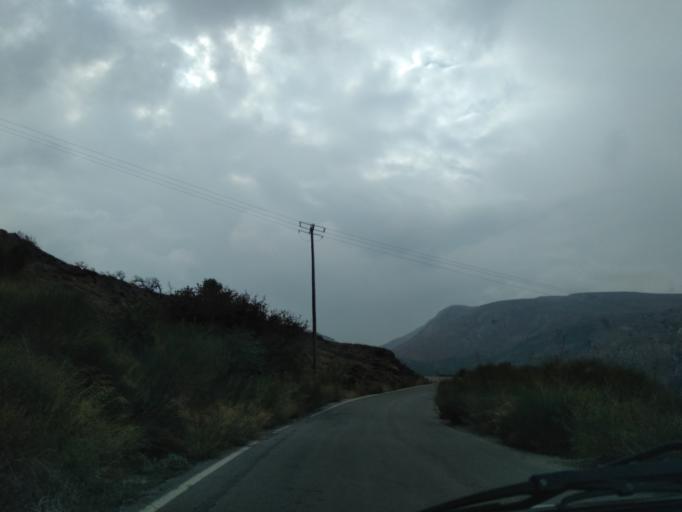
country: GR
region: Crete
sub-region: Nomos Lasithiou
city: Siteia
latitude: 35.1414
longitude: 26.0227
